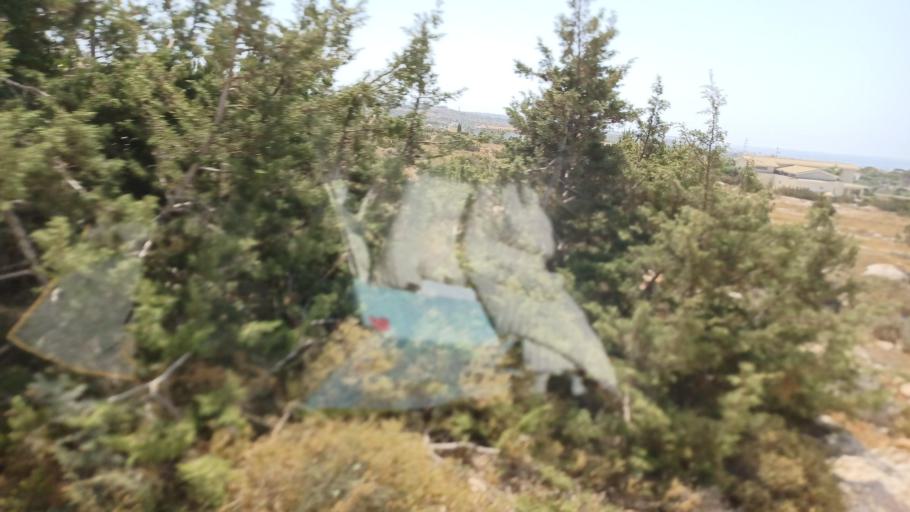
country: CY
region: Ammochostos
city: Paralimni
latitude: 35.0076
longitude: 33.9688
